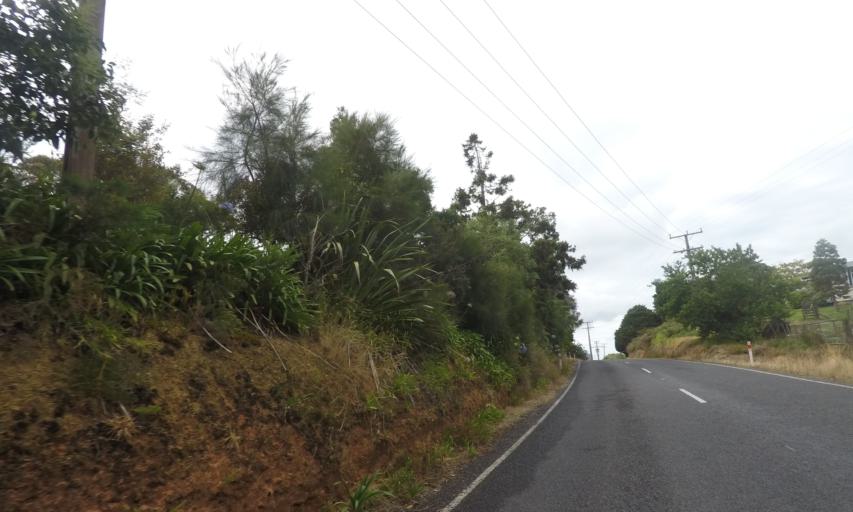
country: NZ
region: Northland
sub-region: Whangarei
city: Whangarei
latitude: -35.7598
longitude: 174.4551
